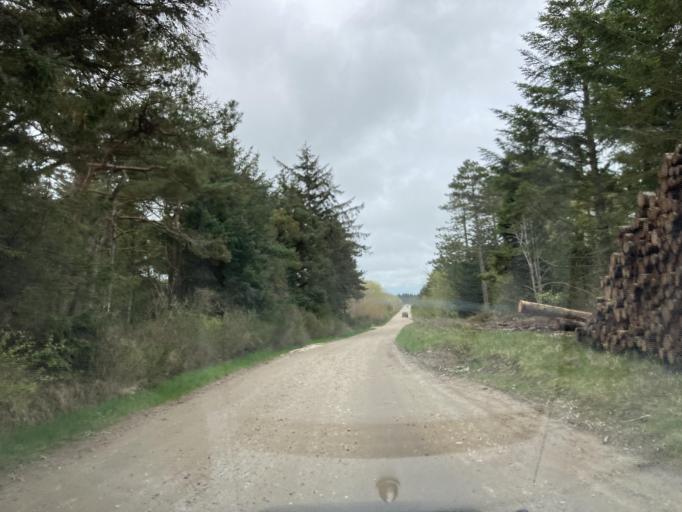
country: DK
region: Central Jutland
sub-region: Lemvig Kommune
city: Thyboron
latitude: 56.8218
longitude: 8.2652
